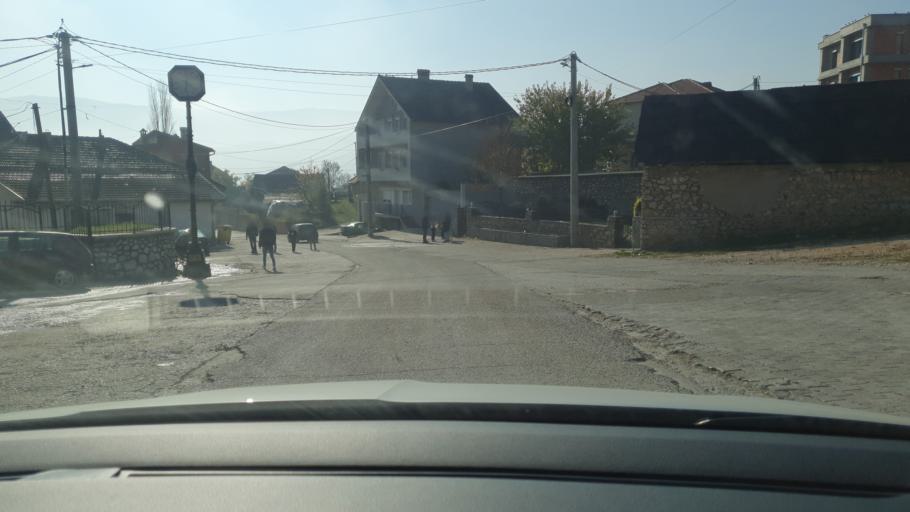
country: MK
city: Bojane
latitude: 41.9999
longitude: 21.1925
